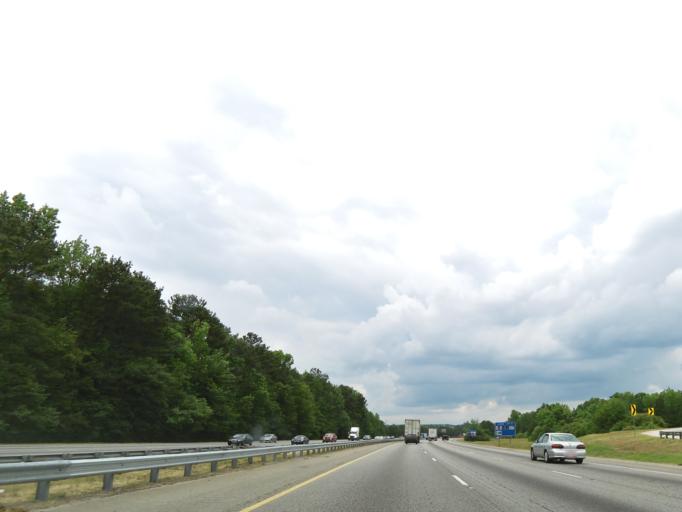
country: US
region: Georgia
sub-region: Douglas County
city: Douglasville
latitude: 33.7328
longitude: -84.7377
